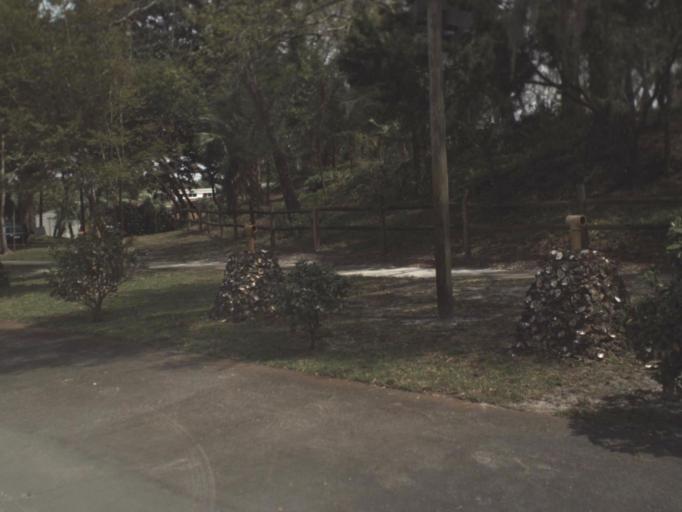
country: US
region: Florida
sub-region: Okaloosa County
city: Fort Walton Beach
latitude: 30.4045
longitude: -86.6077
